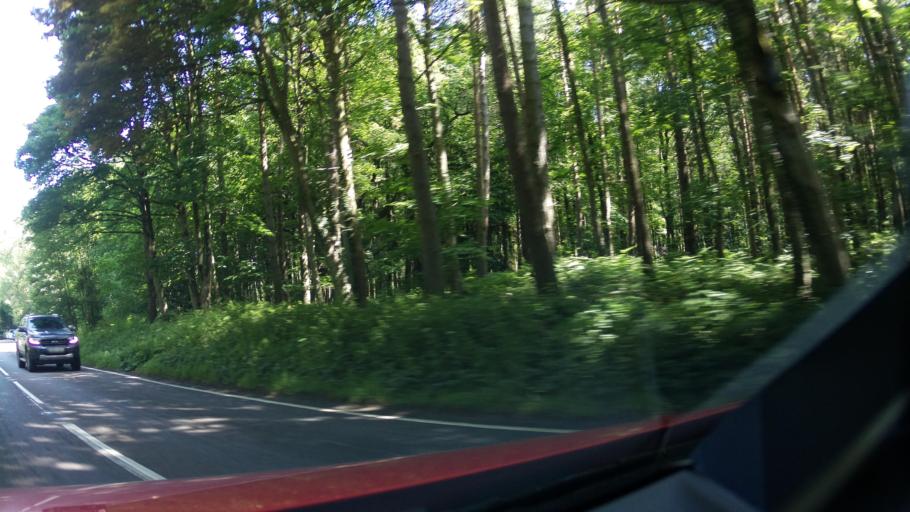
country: GB
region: England
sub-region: North Lincolnshire
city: Manton
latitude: 53.5393
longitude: -0.5767
